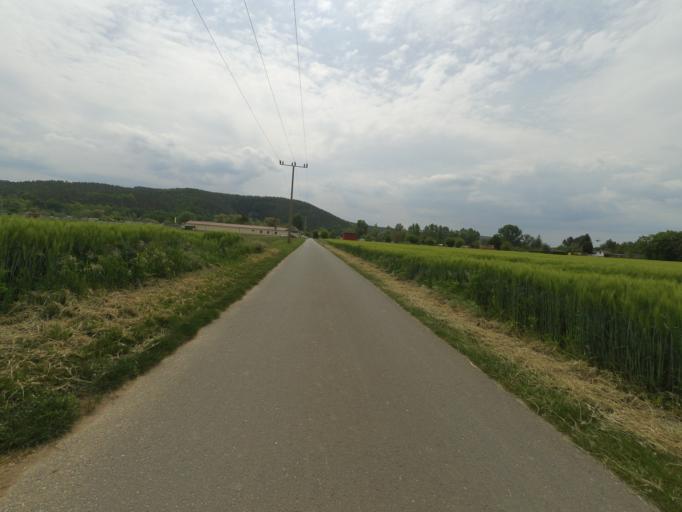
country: DE
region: Thuringia
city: Sulza
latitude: 50.8540
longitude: 11.6130
